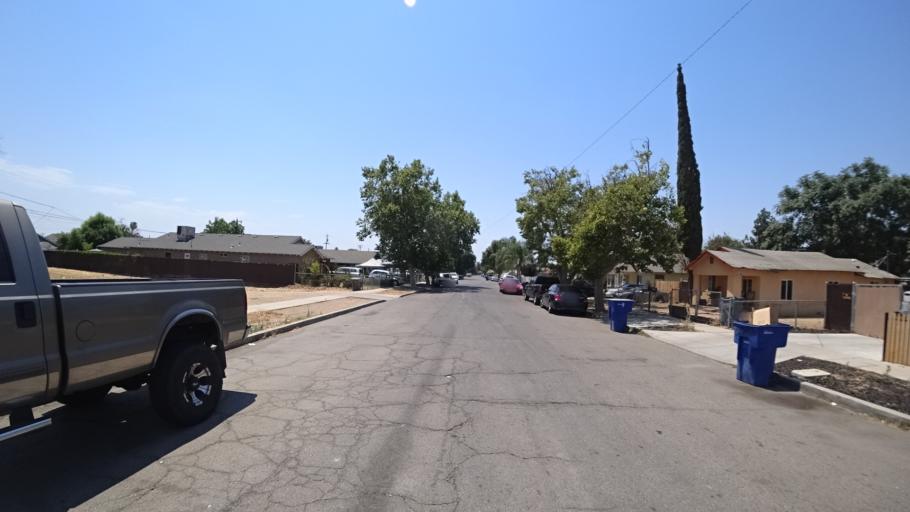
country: US
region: California
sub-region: Fresno County
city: Fresno
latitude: 36.7172
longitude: -119.7942
